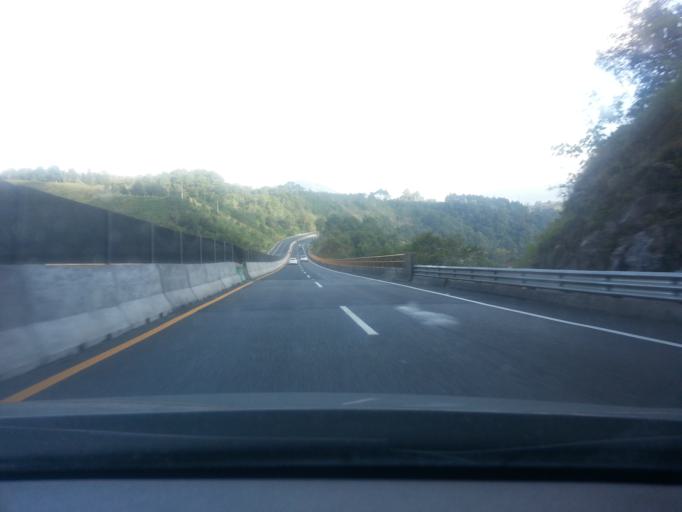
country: MX
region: Puebla
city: Necaxa
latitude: 20.2001
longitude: -98.0320
